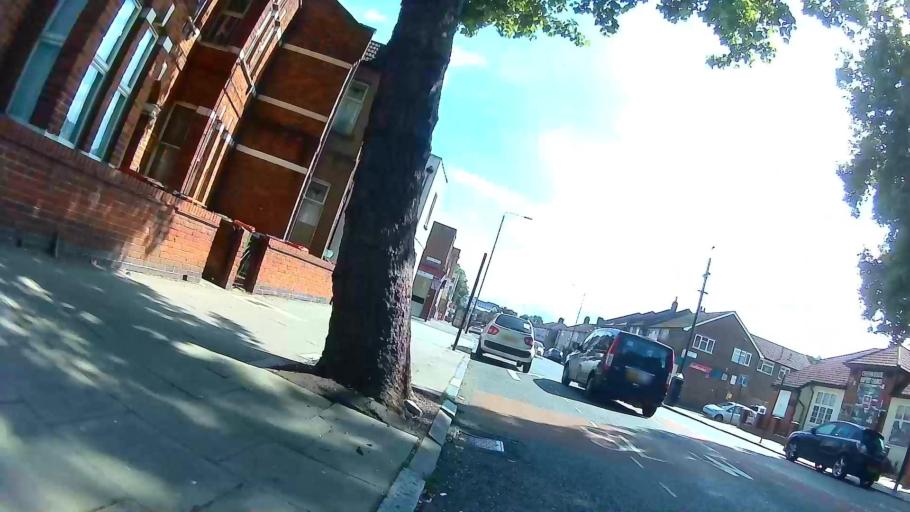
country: GB
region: England
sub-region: Greater London
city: East Ham
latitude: 51.5150
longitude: 0.0319
